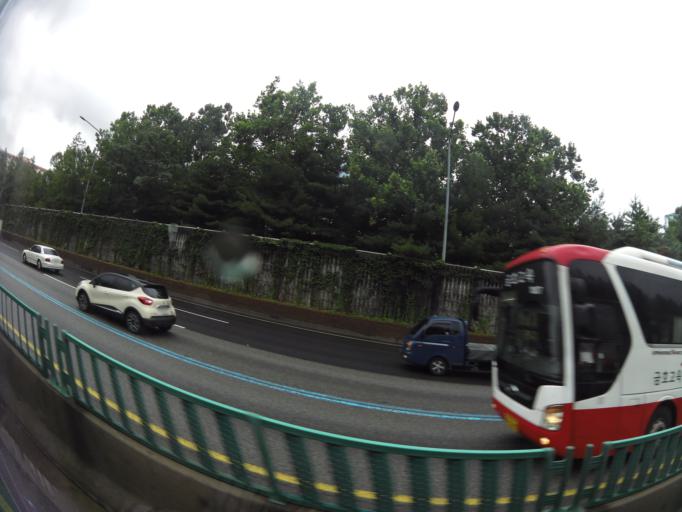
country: KR
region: Seoul
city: Seoul
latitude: 37.4946
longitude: 127.0217
